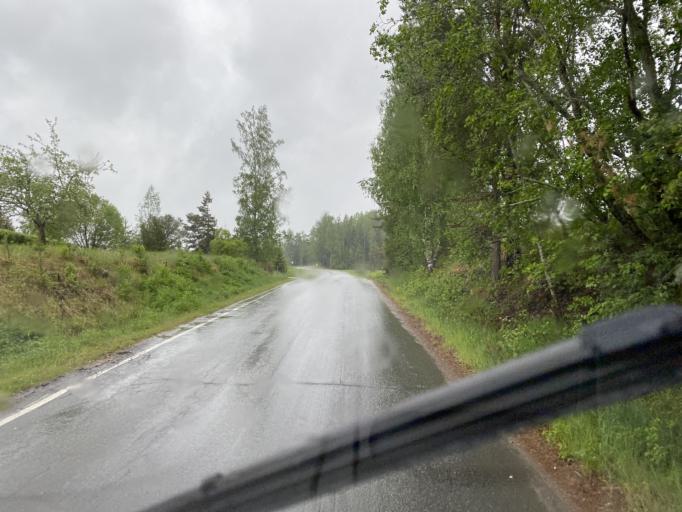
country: FI
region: Haeme
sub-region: Forssa
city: Humppila
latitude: 61.0958
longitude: 23.3167
